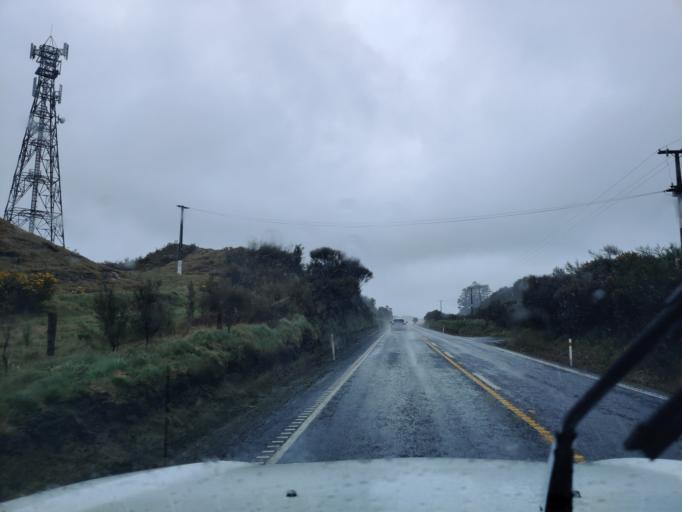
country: NZ
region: Bay of Plenty
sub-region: Rotorua District
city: Rotorua
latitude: -38.0421
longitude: 176.0608
